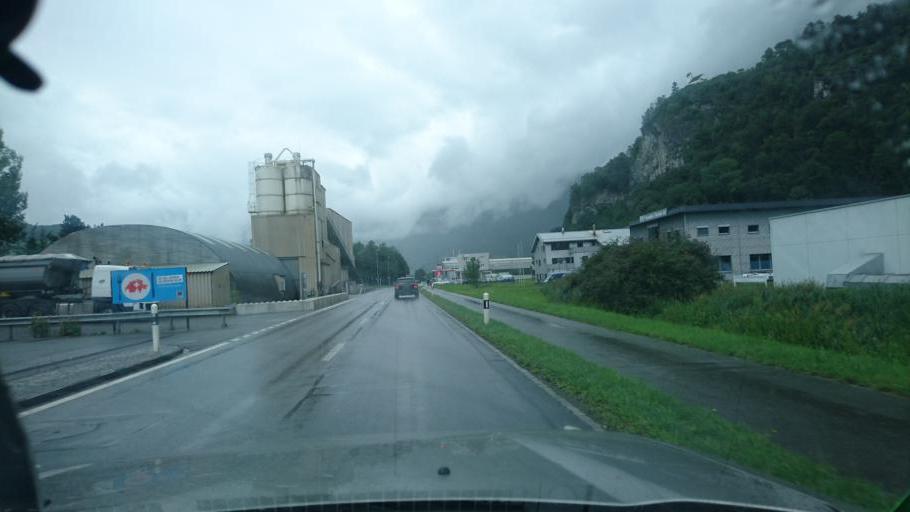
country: CH
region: Saint Gallen
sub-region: Wahlkreis Sarganserland
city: Flums
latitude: 47.0973
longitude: 9.3525
